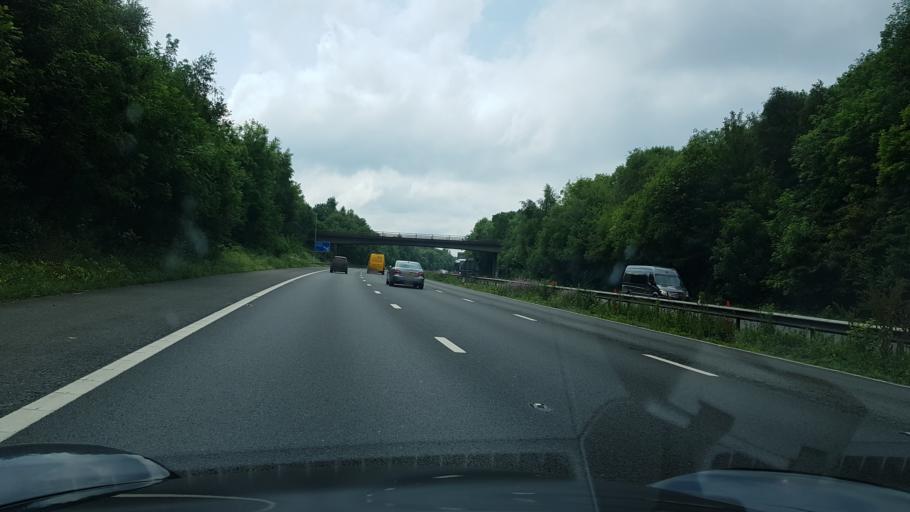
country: GB
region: England
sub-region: West Sussex
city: Maidenbower
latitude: 51.1172
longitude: -0.1374
